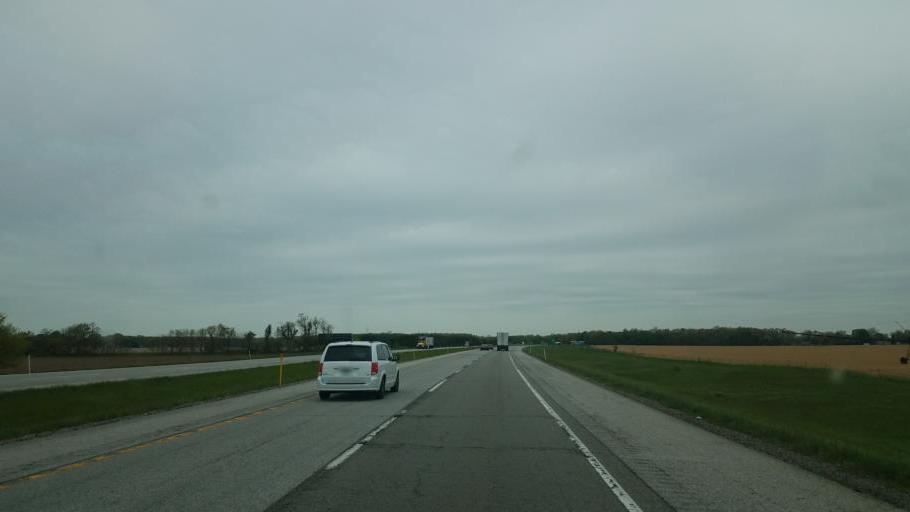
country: US
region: Michigan
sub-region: Saint Joseph County
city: White Pigeon
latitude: 41.7519
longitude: -85.6277
